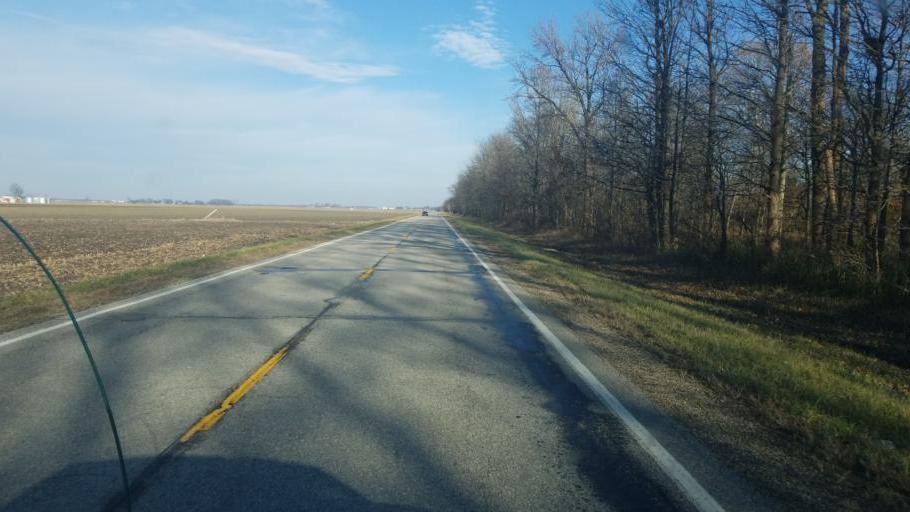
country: US
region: Illinois
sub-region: Edwards County
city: Grayville
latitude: 38.3262
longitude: -87.9118
